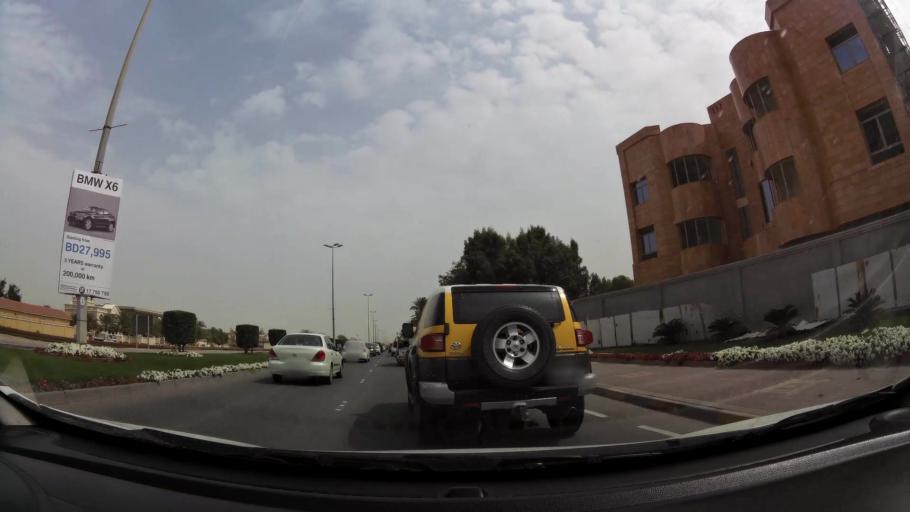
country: BH
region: Northern
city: Ar Rifa'
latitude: 26.1330
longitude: 50.5401
